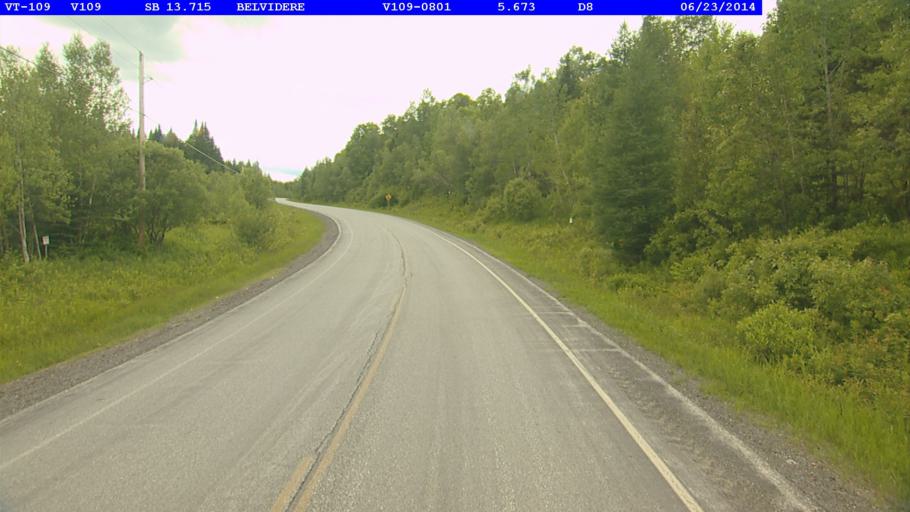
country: US
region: Vermont
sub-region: Lamoille County
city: Johnson
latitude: 44.7624
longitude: -72.6439
